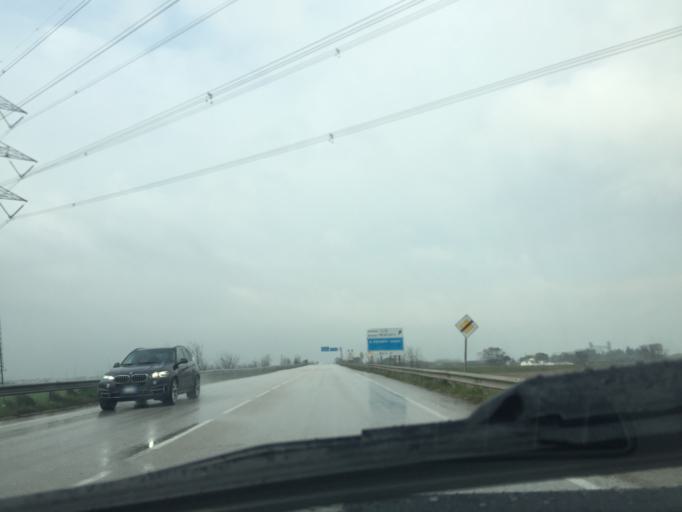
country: IT
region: Apulia
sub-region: Provincia di Foggia
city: Foggia
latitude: 41.4980
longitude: 15.5260
